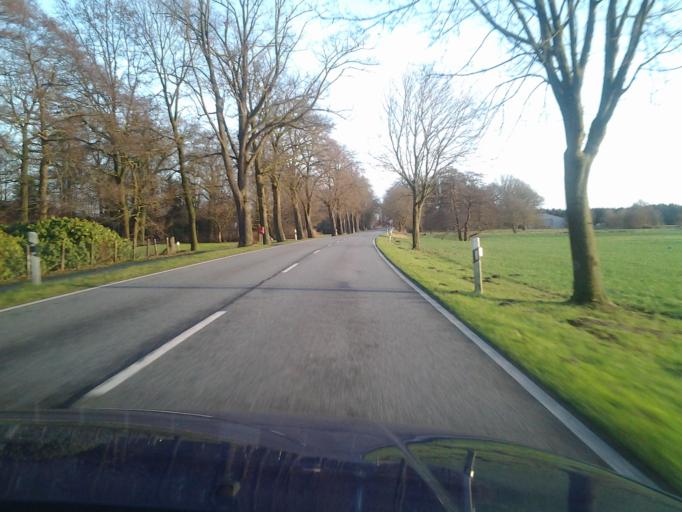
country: DE
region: Lower Saxony
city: Lilienthal
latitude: 53.1757
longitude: 8.8895
